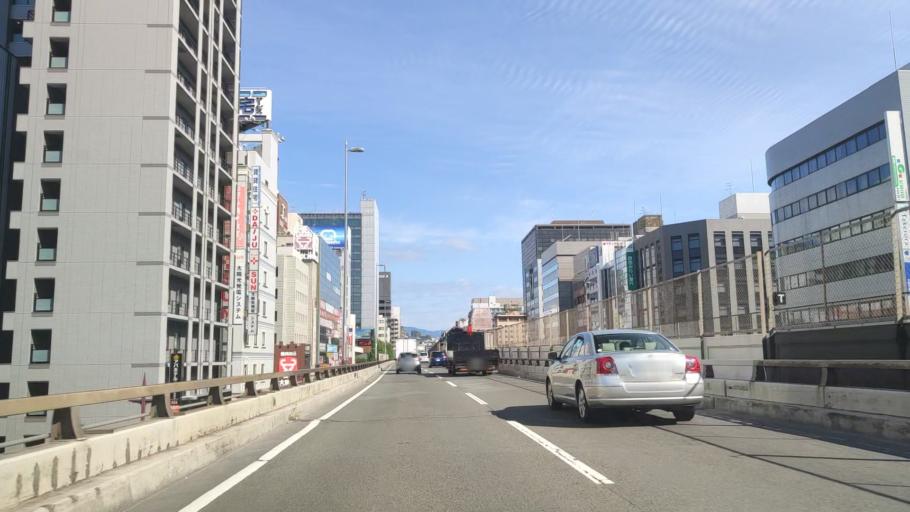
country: JP
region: Osaka
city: Suita
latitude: 34.7566
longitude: 135.4968
